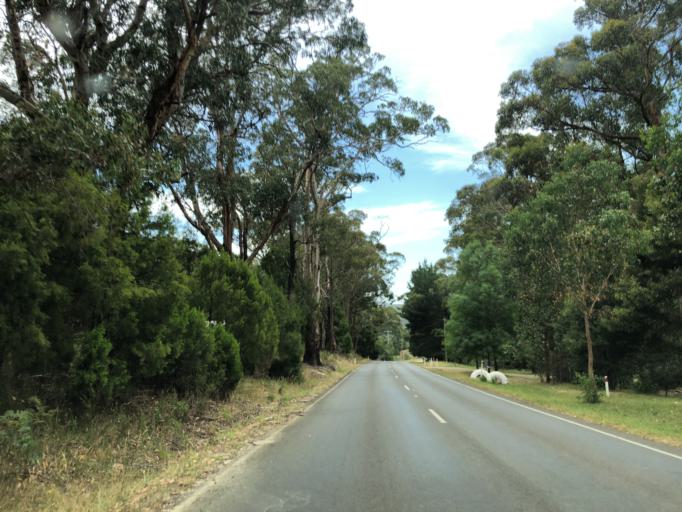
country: AU
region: Victoria
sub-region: Moorabool
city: Bacchus Marsh
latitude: -37.4778
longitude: 144.3052
